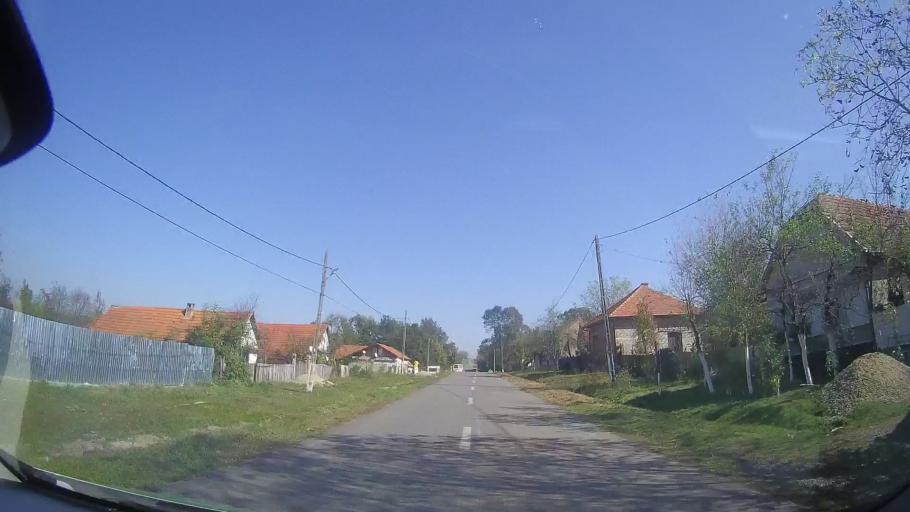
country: RO
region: Timis
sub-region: Comuna Balint
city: Balint
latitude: 45.8433
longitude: 21.8602
